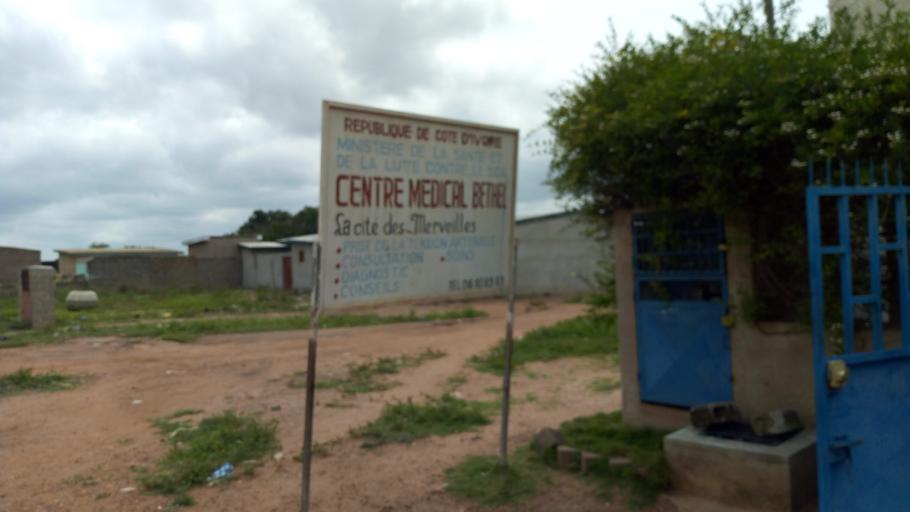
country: CI
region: Vallee du Bandama
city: Bouake
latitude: 7.7271
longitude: -5.0499
